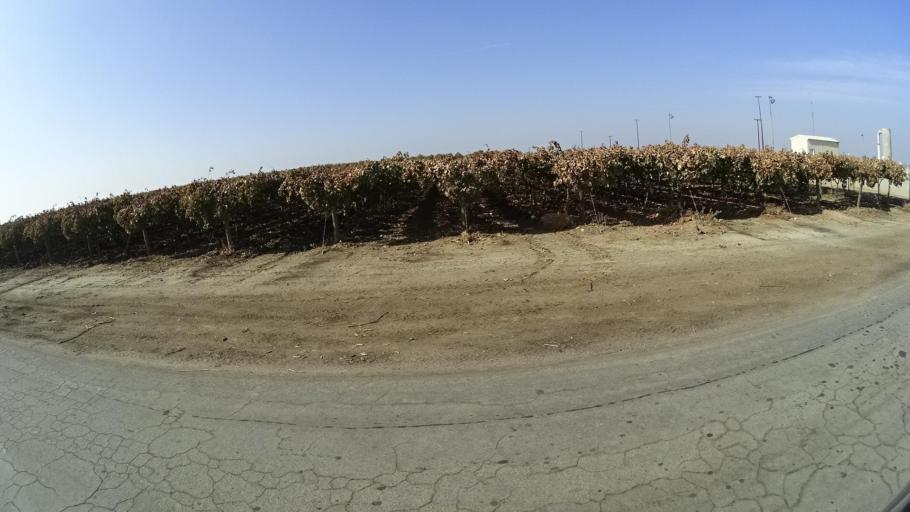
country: US
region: California
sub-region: Kern County
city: McFarland
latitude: 35.6303
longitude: -119.1866
